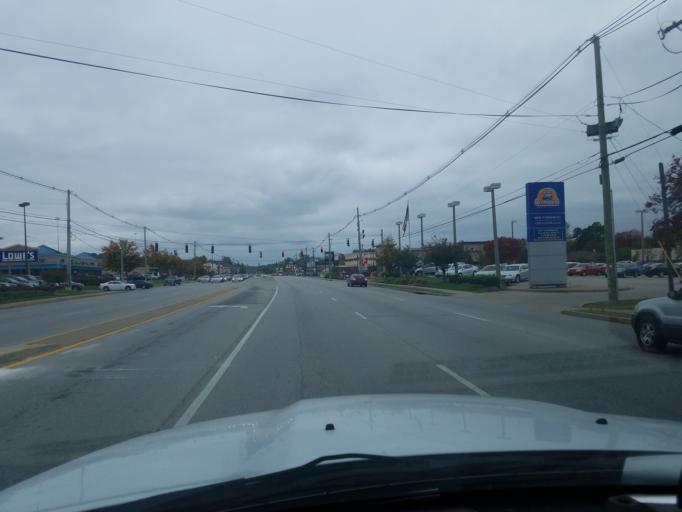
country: US
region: Kentucky
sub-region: Jefferson County
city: Pleasure Ridge Park
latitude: 38.1550
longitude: -85.8352
